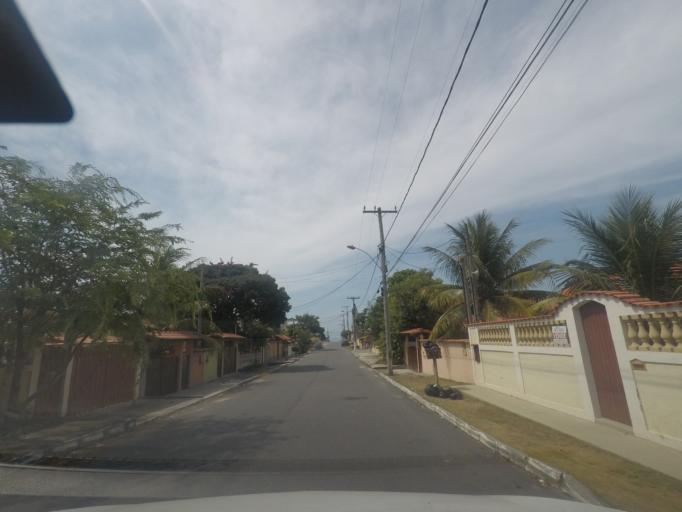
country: BR
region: Rio de Janeiro
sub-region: Marica
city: Marica
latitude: -22.9546
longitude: -42.7498
